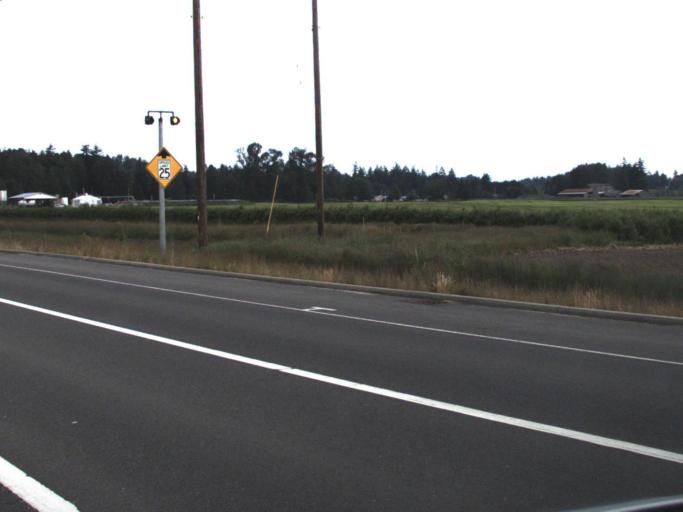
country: US
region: Washington
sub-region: Whatcom County
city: Lynden
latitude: 48.9969
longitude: -122.4851
